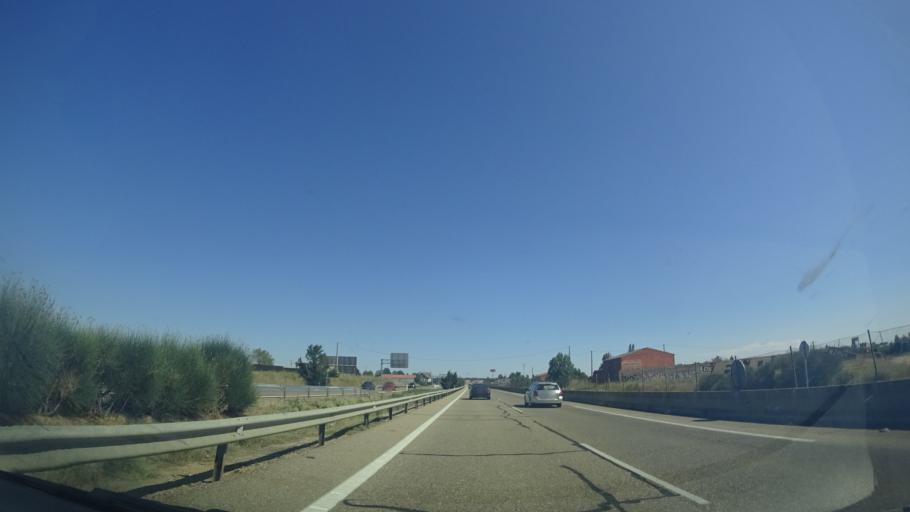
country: ES
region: Castille and Leon
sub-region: Provincia de Zamora
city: San Esteban del Molar
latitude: 41.9413
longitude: -5.5522
